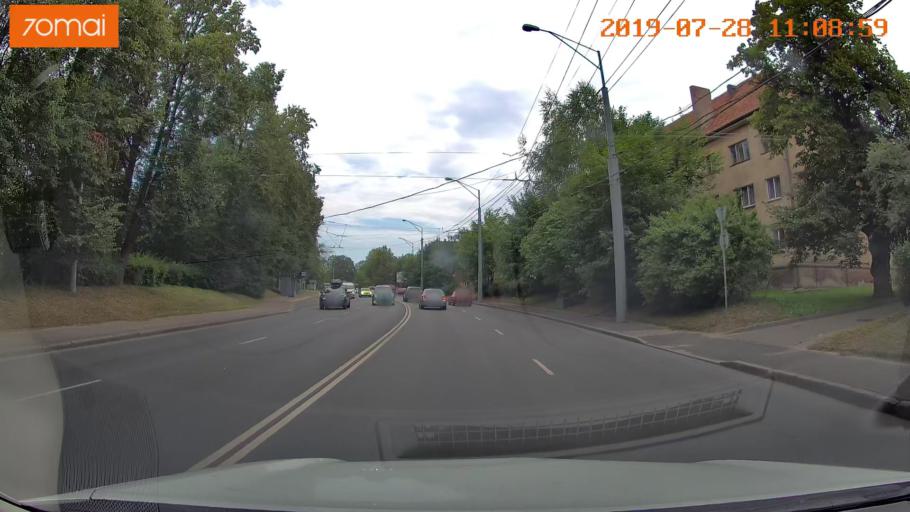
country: RU
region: Kaliningrad
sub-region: Gorod Kaliningrad
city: Kaliningrad
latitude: 54.7116
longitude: 20.4496
